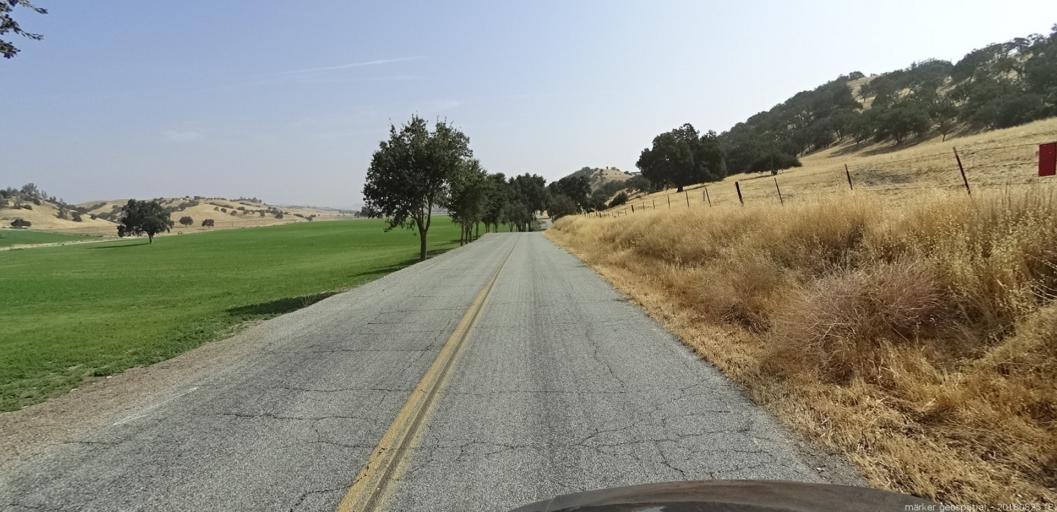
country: US
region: California
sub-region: San Luis Obispo County
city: San Miguel
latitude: 35.8091
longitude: -120.6711
